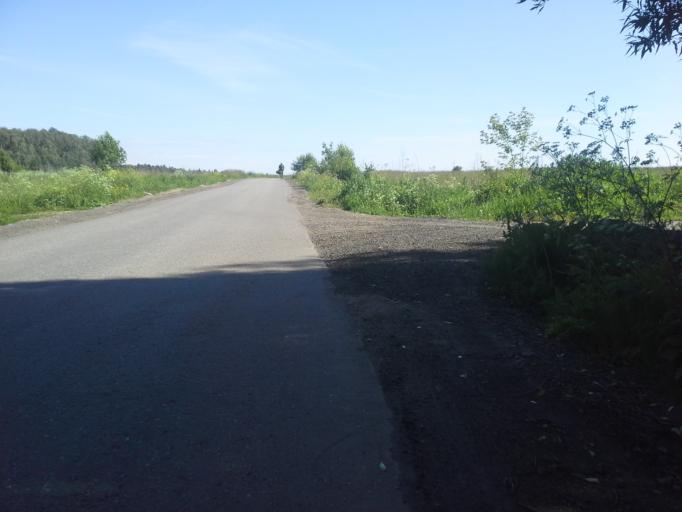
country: RU
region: Moskovskaya
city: Dubrovitsy
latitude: 55.4621
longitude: 37.4426
